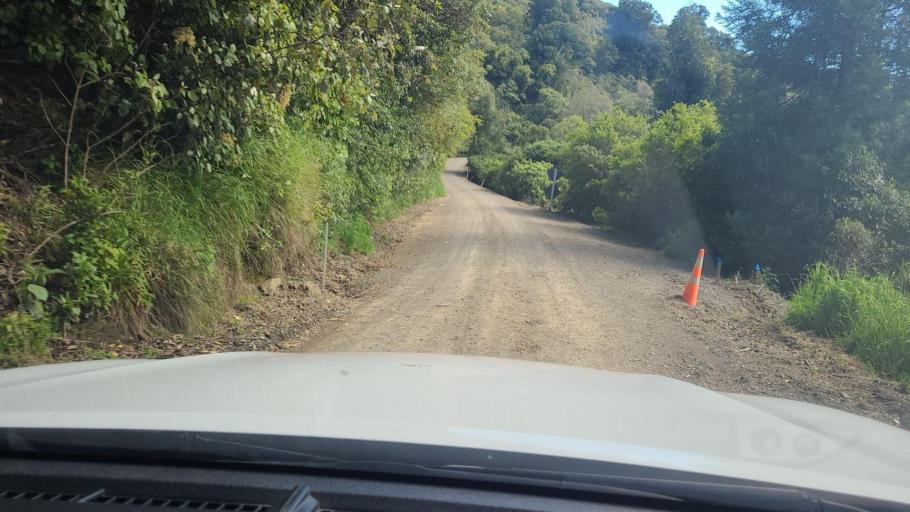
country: NZ
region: Hawke's Bay
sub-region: Napier City
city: Napier
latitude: -39.1004
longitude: 176.8022
